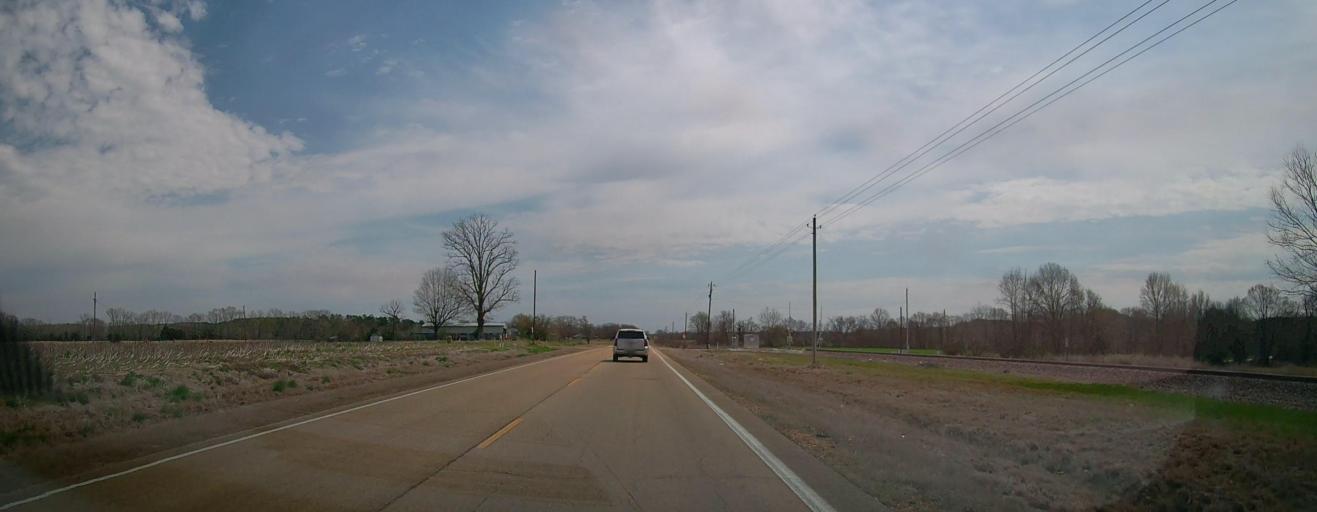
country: US
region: Mississippi
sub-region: Benton County
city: Ashland
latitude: 34.6232
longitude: -89.2426
